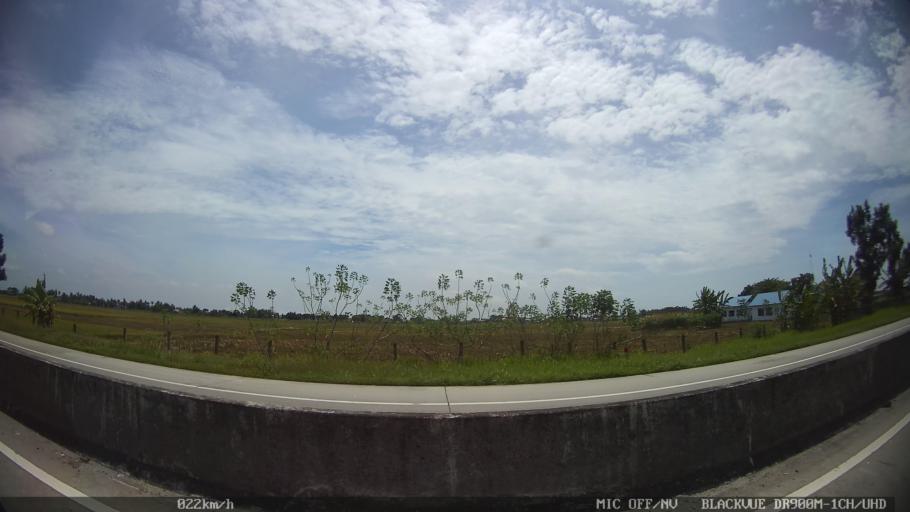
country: ID
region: North Sumatra
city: Perbaungan
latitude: 3.5395
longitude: 98.8924
